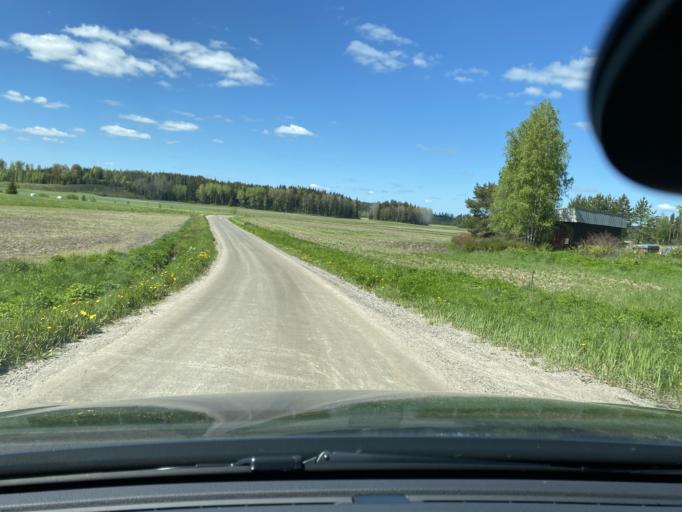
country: FI
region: Varsinais-Suomi
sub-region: Salo
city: Halikko
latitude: 60.3442
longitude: 22.9032
